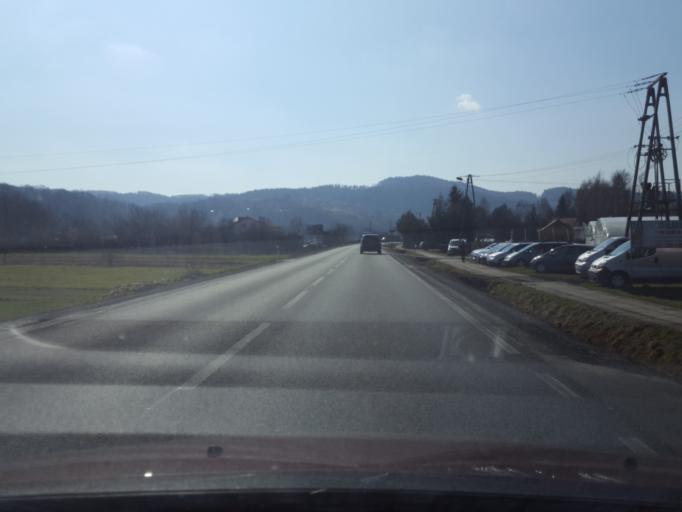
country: PL
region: Lesser Poland Voivodeship
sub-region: Powiat brzeski
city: Czchow
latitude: 49.8268
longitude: 20.6785
